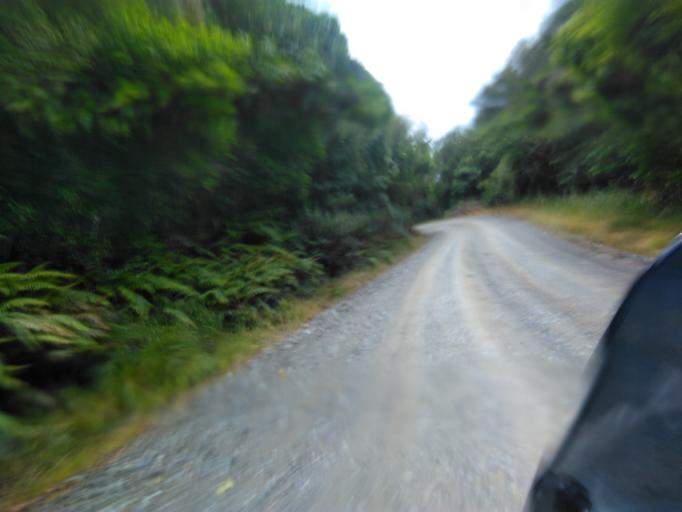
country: NZ
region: Gisborne
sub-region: Gisborne District
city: Gisborne
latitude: -38.1712
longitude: 178.1347
